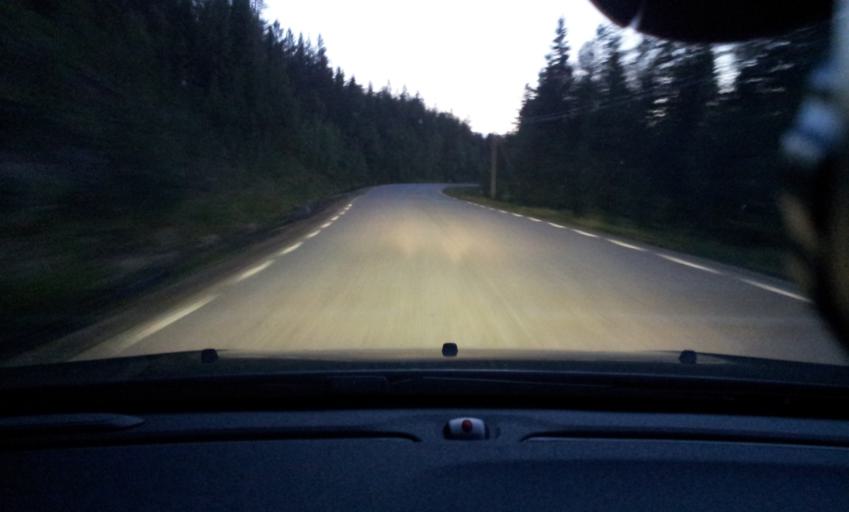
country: SE
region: Jaemtland
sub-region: Bergs Kommun
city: Hoverberg
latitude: 62.7409
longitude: 14.5853
